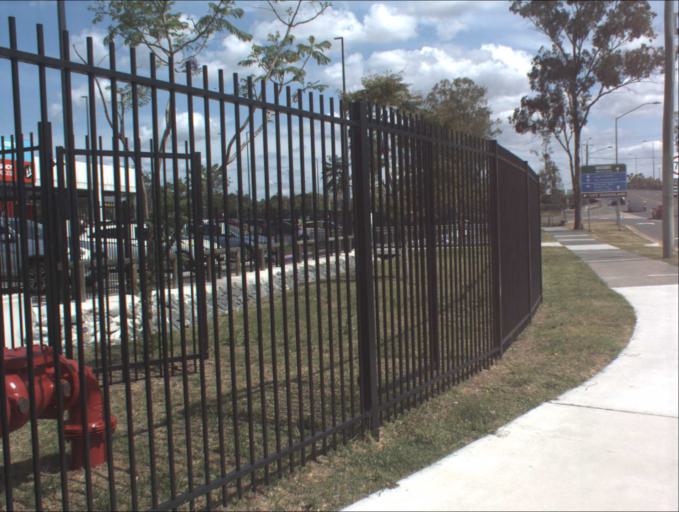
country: AU
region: Queensland
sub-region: Logan
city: Slacks Creek
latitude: -27.6688
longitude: 153.1395
